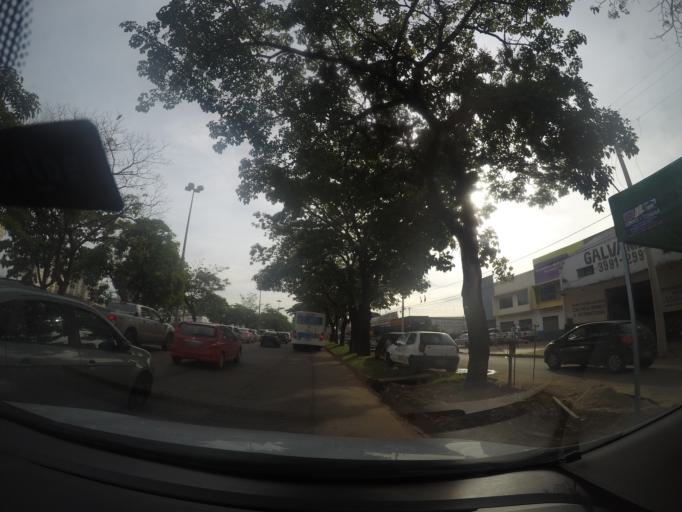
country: BR
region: Goias
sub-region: Goiania
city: Goiania
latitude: -16.6968
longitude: -49.3276
